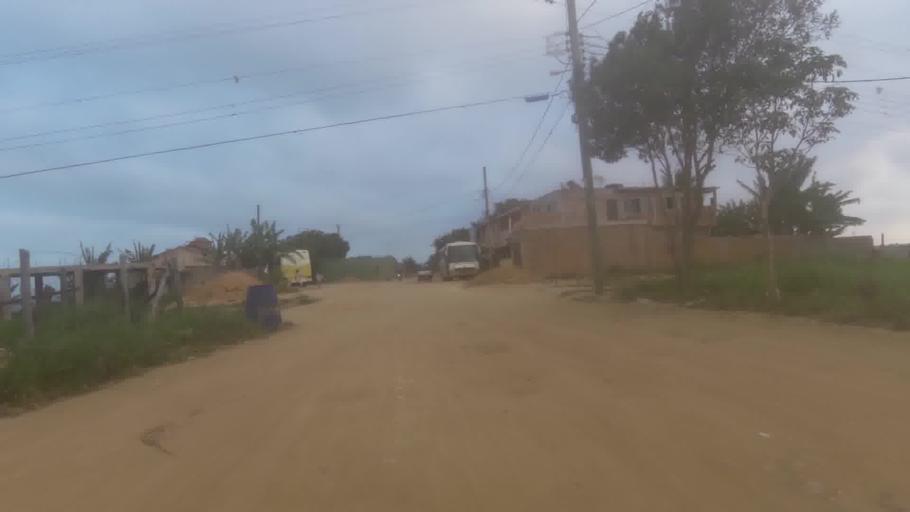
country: BR
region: Espirito Santo
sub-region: Marataizes
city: Marataizes
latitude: -21.0348
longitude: -40.8236
